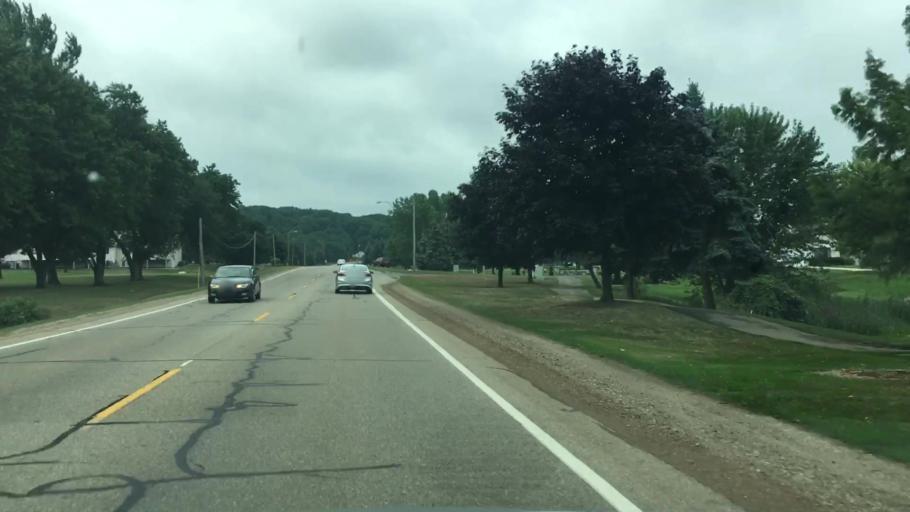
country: US
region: Michigan
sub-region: Ottawa County
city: Jenison
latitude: 42.8778
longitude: -85.8168
